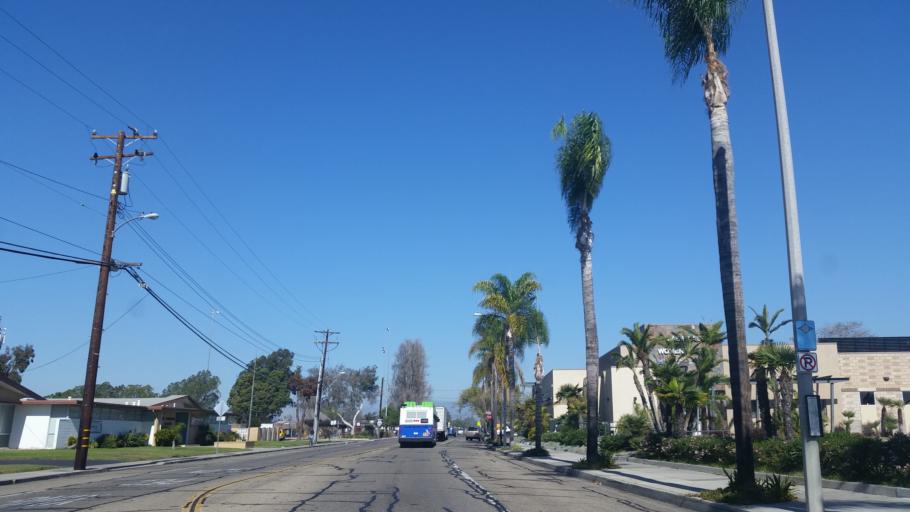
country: US
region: California
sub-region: Ventura County
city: Oxnard
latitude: 34.1764
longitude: -119.1813
